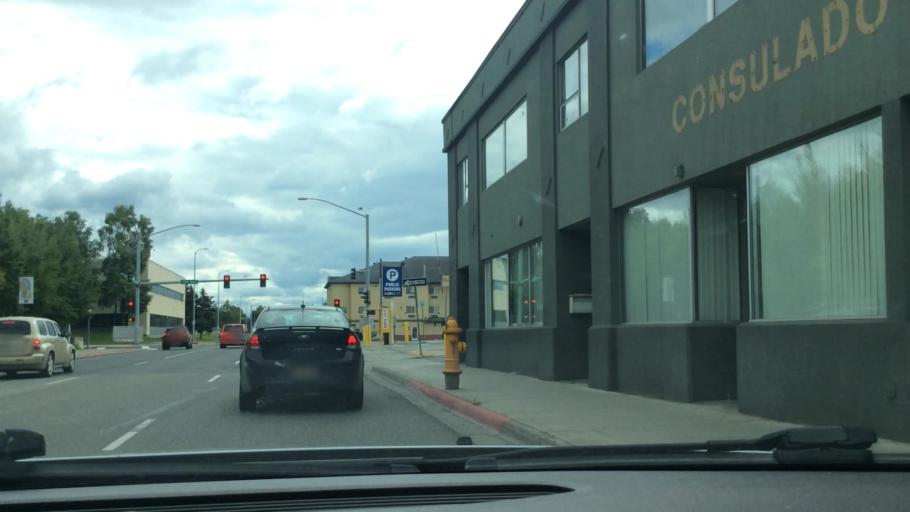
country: US
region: Alaska
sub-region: Anchorage Municipality
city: Anchorage
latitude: 61.2163
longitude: -149.8874
